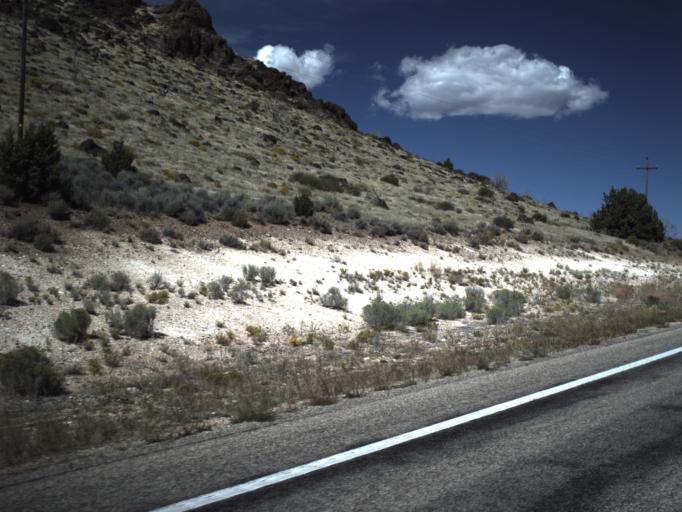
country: US
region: Utah
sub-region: Washington County
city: Enterprise
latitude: 37.3754
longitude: -113.6562
